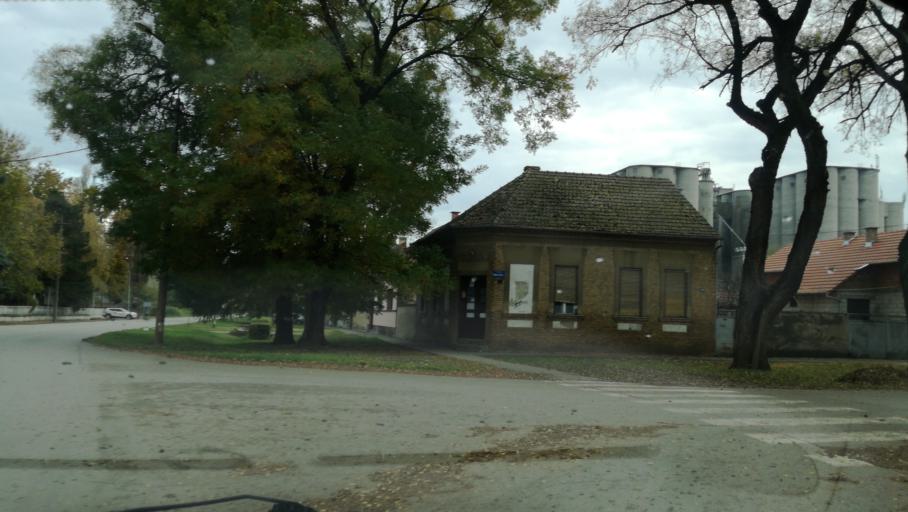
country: RS
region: Autonomna Pokrajina Vojvodina
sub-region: Severnobanatski Okrug
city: Kikinda
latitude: 45.8411
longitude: 20.4837
